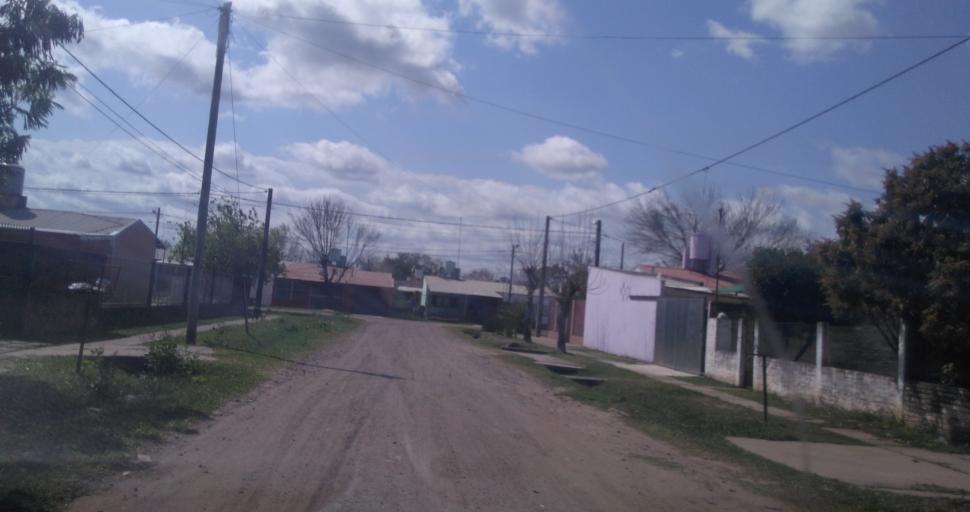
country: AR
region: Chaco
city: Fontana
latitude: -27.4318
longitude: -59.0333
